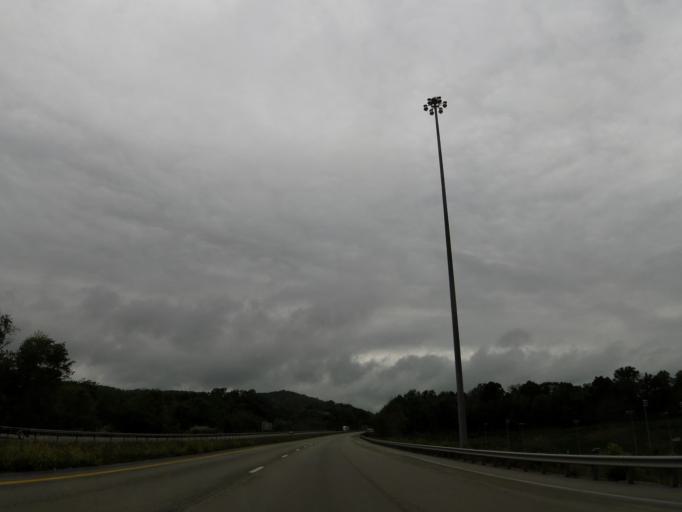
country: US
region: Kentucky
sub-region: Whitley County
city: Williamsburg
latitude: 36.7282
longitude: -84.1698
